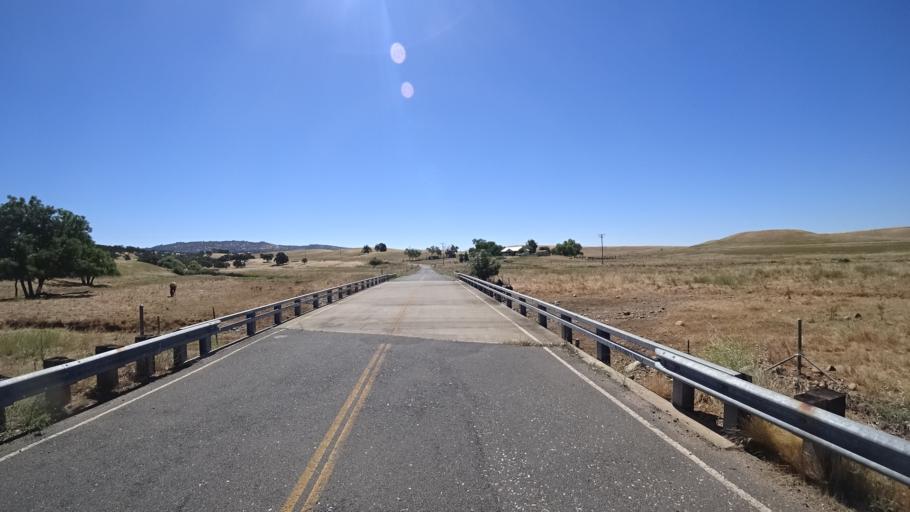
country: US
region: California
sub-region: Calaveras County
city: Rancho Calaveras
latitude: 38.0160
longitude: -120.8278
